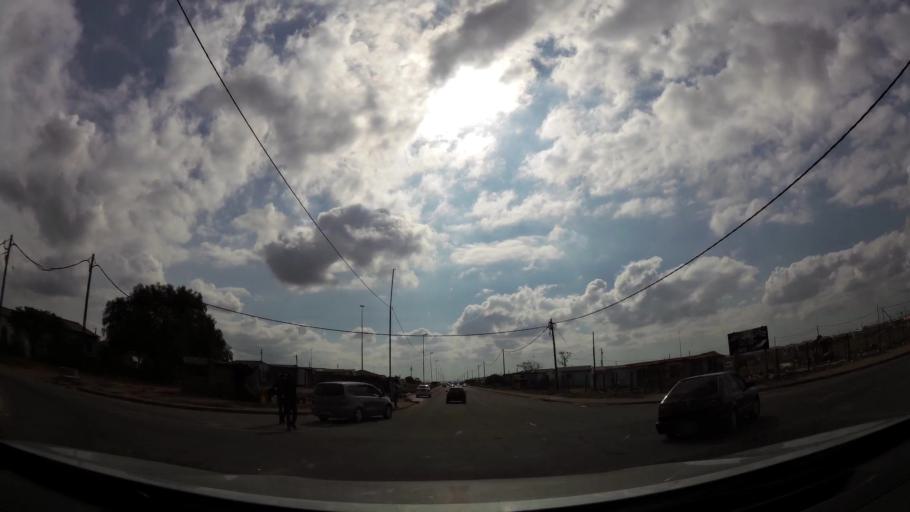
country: ZA
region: Eastern Cape
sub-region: Nelson Mandela Bay Metropolitan Municipality
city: Port Elizabeth
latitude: -33.7953
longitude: 25.5826
